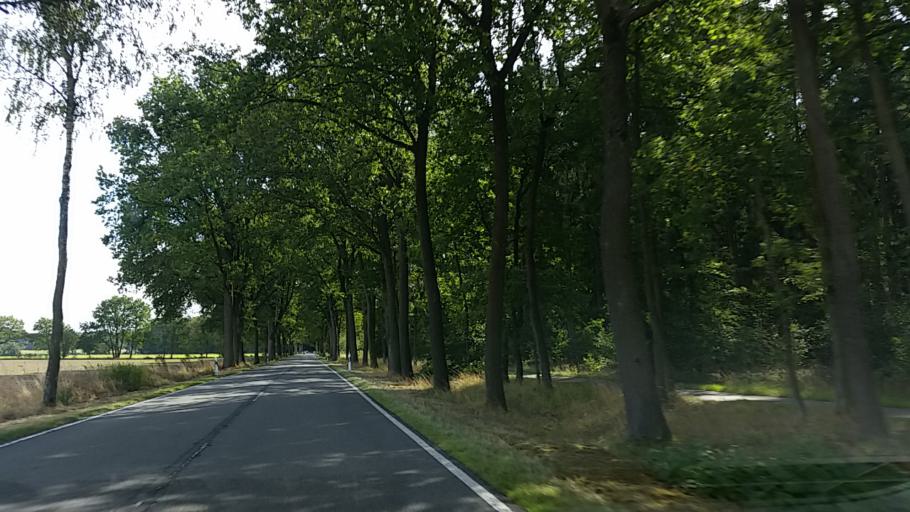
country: DE
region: Lower Saxony
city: Ebstorf
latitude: 53.0468
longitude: 10.4130
